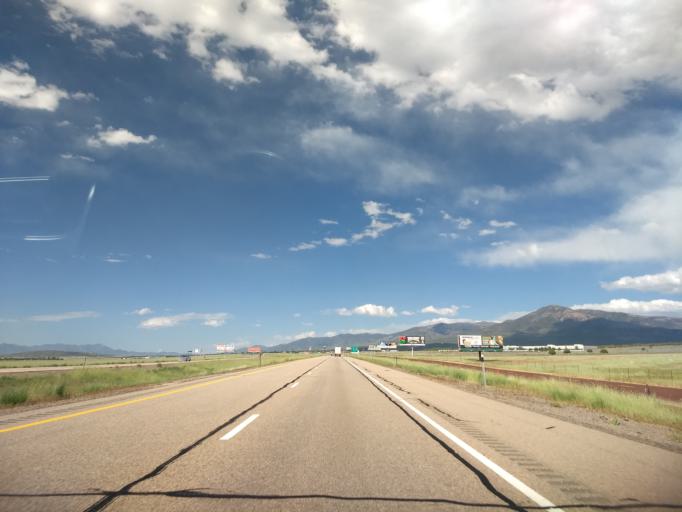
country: US
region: Utah
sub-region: Millard County
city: Fillmore
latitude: 38.9350
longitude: -112.3615
